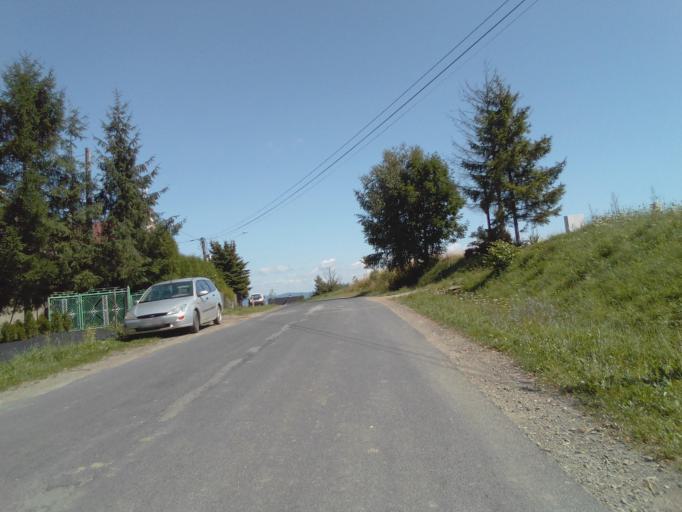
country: PL
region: Subcarpathian Voivodeship
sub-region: Powiat krosnienski
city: Jedlicze
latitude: 49.6799
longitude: 21.6141
